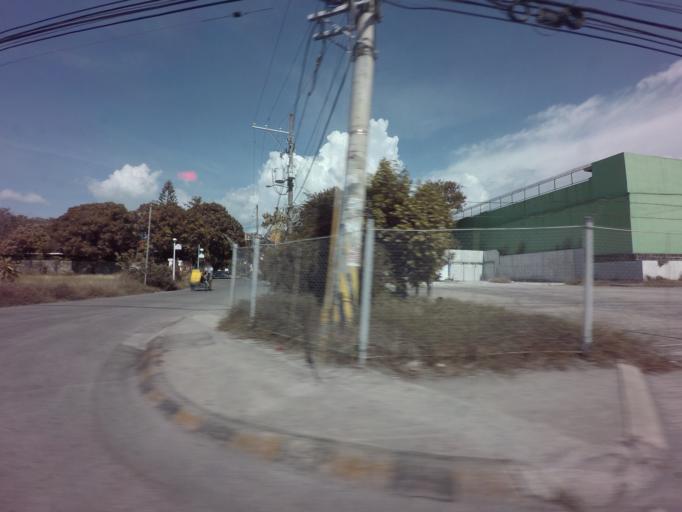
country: PH
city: Sambayanihan People's Village
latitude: 14.4402
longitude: 121.0051
